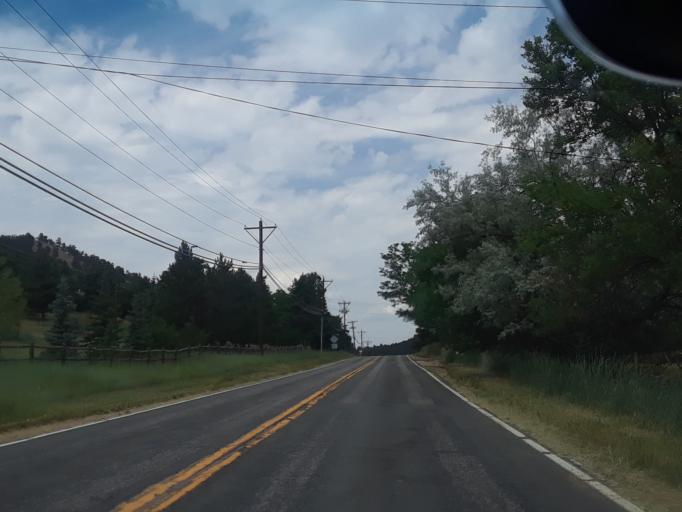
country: US
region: Colorado
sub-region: Boulder County
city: Boulder
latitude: 40.0766
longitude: -105.3013
